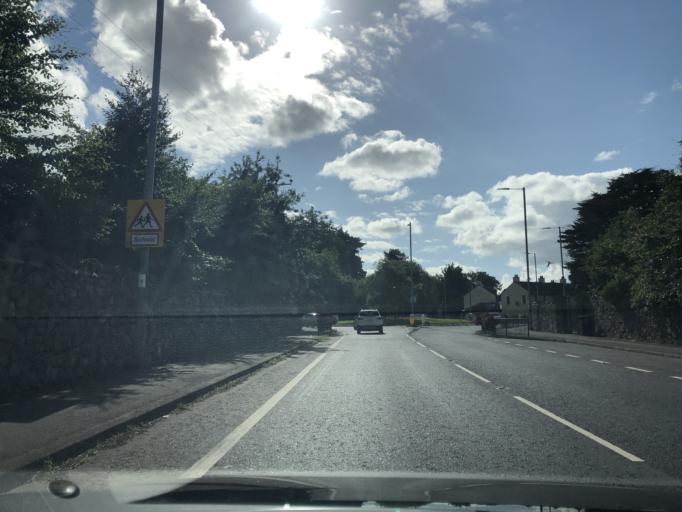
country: GB
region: Northern Ireland
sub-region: Ards District
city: Comber
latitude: 54.5471
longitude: -5.7416
